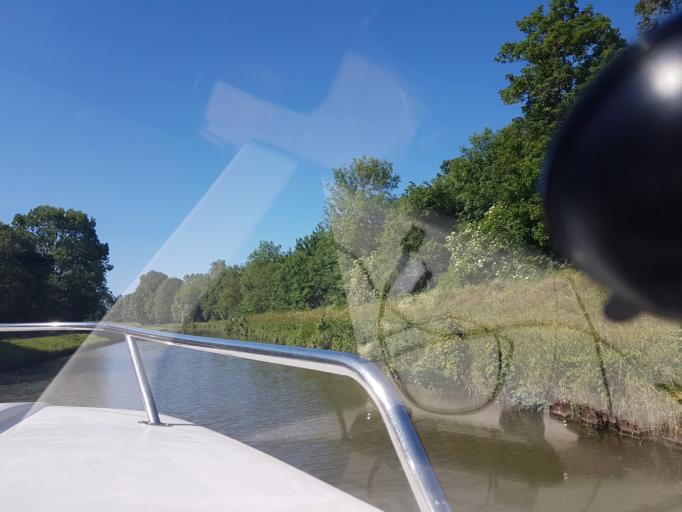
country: FR
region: Bourgogne
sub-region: Departement de la Nievre
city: Clamecy
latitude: 47.5371
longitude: 3.6003
